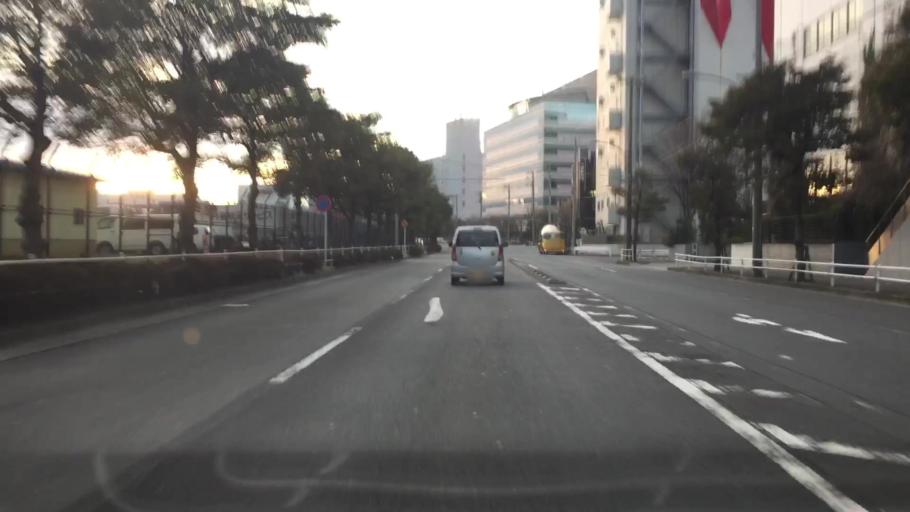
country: JP
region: Tokyo
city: Urayasu
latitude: 35.6421
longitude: 139.8118
